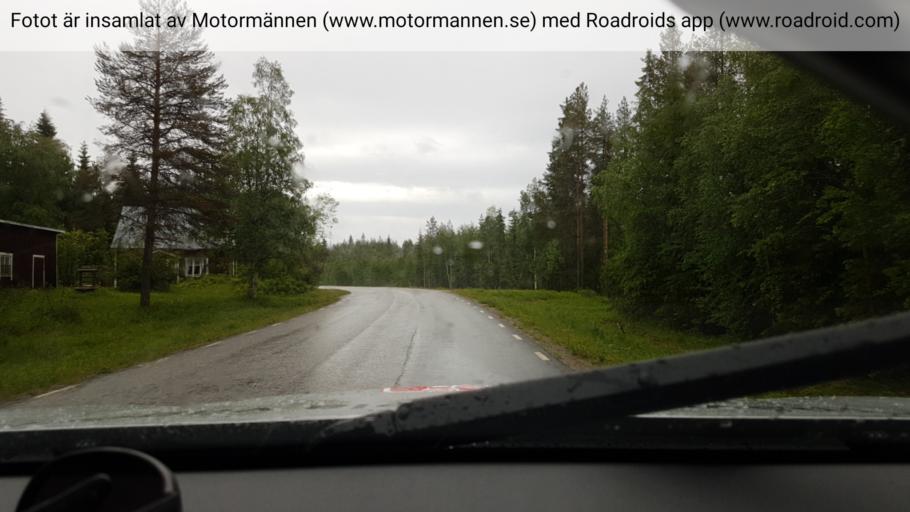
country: SE
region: Vaesterbotten
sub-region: Sorsele Kommun
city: Sorsele
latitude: 65.3057
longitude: 17.7158
